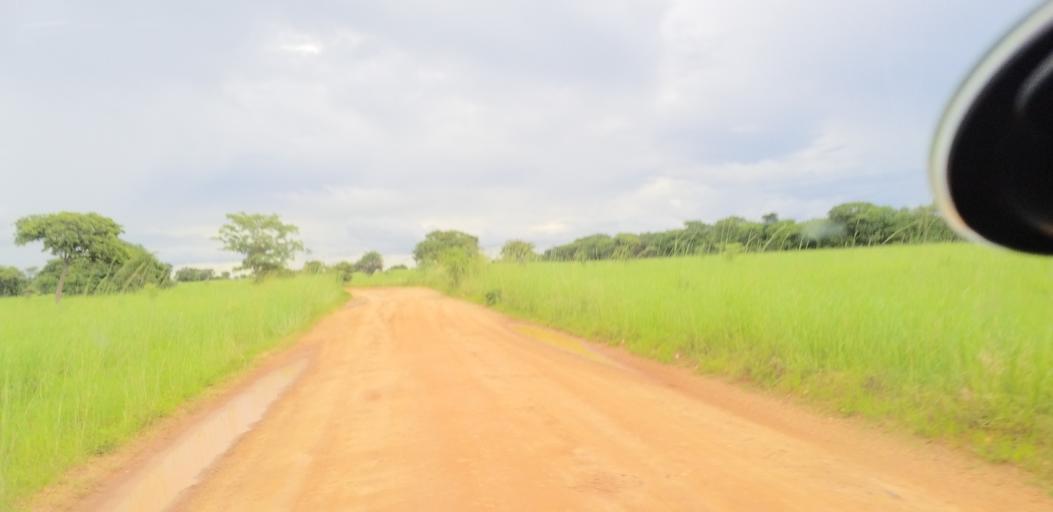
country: ZM
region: Lusaka
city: Chongwe
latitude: -15.1621
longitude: 28.4713
